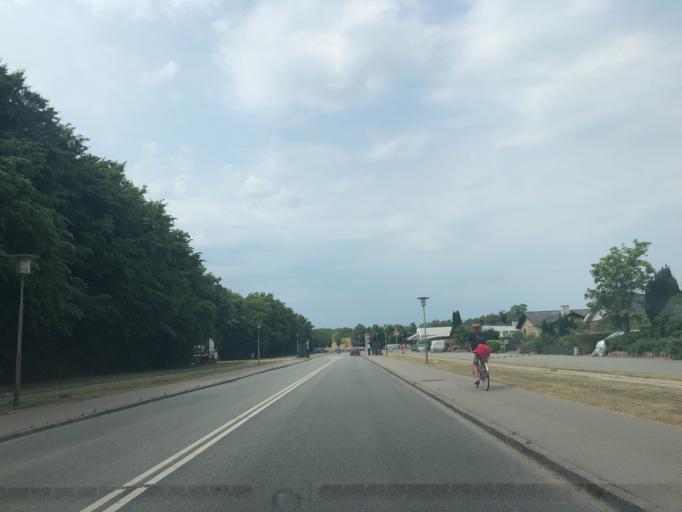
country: DK
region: Zealand
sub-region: Koge Kommune
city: Koge
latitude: 55.4515
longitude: 12.1688
